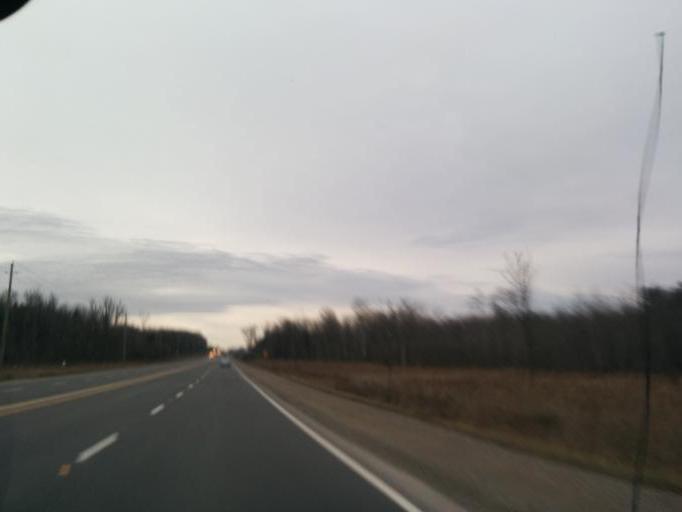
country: CA
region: Ontario
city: Shelburne
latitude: 44.0844
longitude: -80.1748
